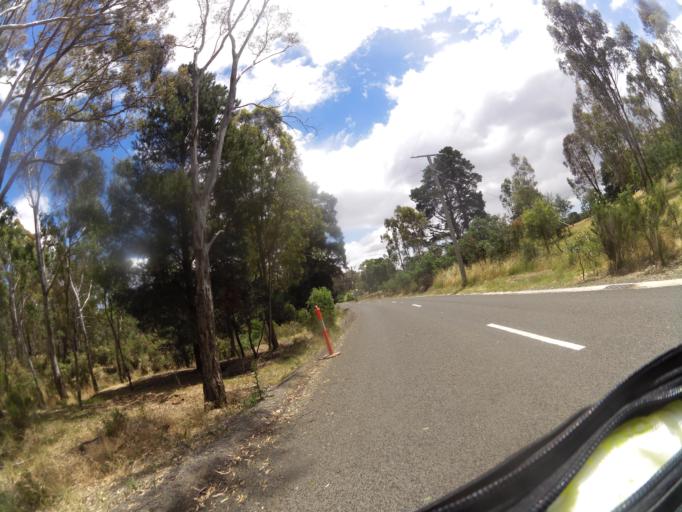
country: AU
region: Victoria
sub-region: Mount Alexander
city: Castlemaine
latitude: -37.0286
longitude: 144.2437
